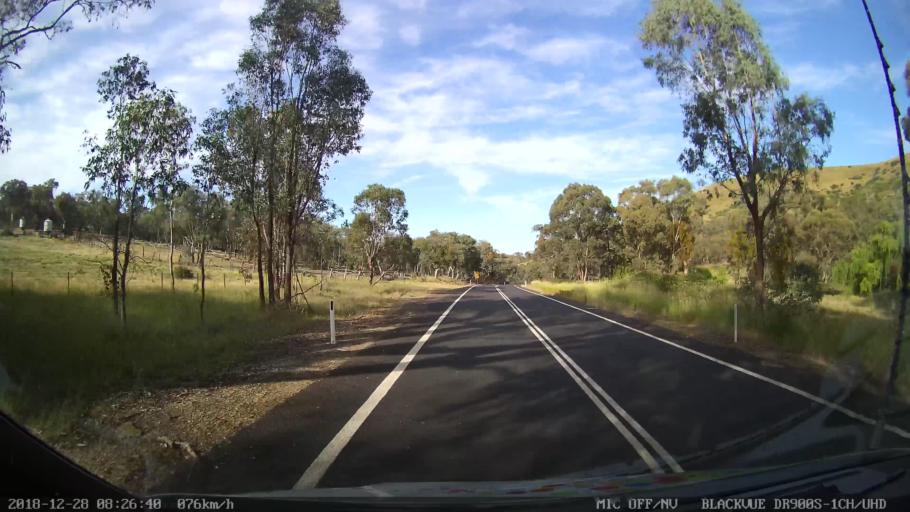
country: AU
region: New South Wales
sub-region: Blayney
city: Blayney
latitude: -33.9381
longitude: 149.3452
